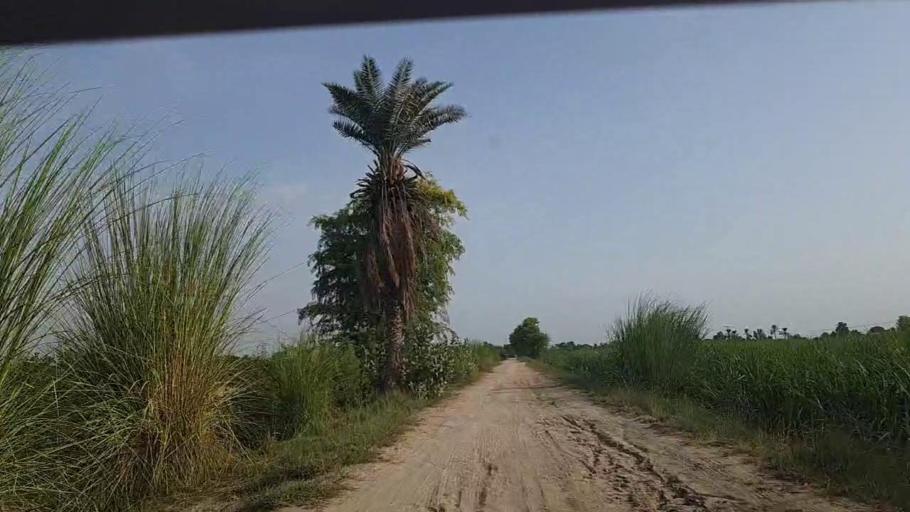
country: PK
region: Sindh
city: Ghotki
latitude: 28.0006
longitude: 69.2618
